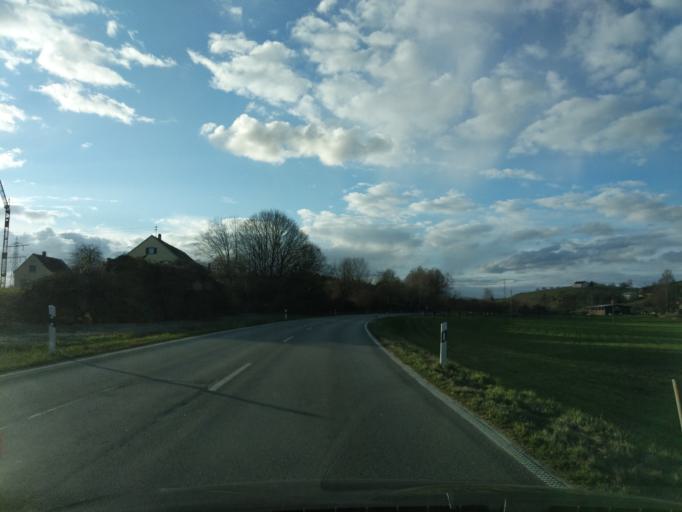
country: DE
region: Baden-Wuerttemberg
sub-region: Tuebingen Region
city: Markdorf
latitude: 47.7240
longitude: 9.3718
